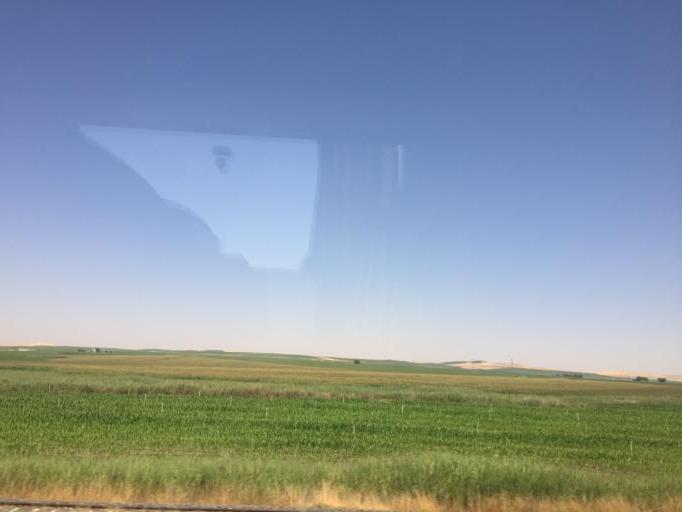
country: TR
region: Diyarbakir
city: Tepe
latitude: 37.8510
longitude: 40.7642
